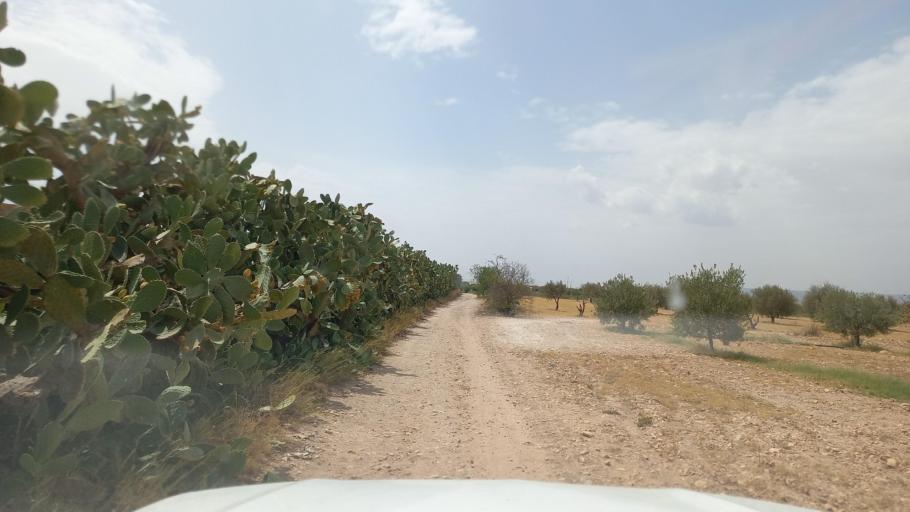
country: TN
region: Al Qasrayn
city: Kasserine
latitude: 35.2733
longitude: 9.0251
